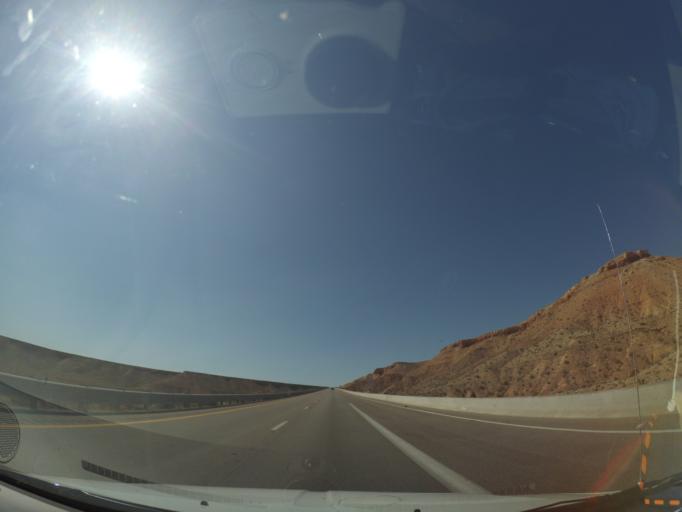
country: US
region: Nevada
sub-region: Clark County
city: Bunkerville
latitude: 36.7731
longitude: -114.2420
